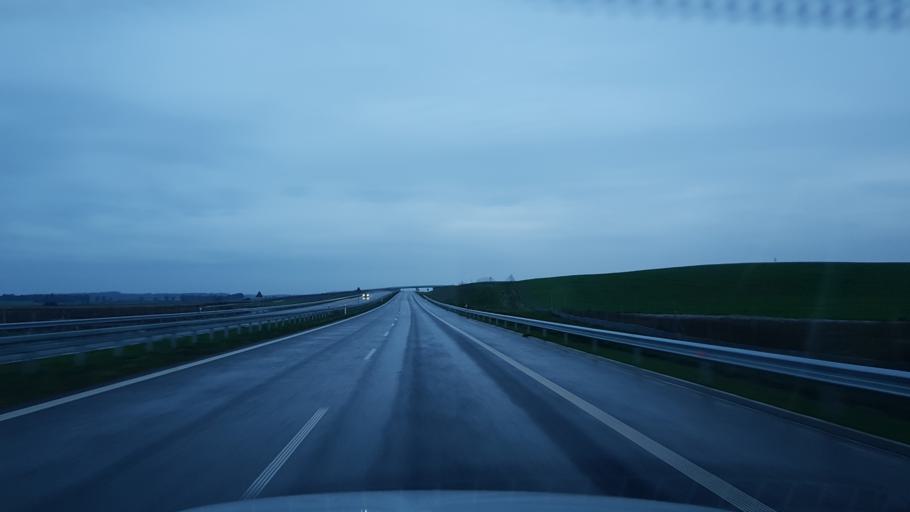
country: PL
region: West Pomeranian Voivodeship
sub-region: Powiat gryficki
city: Brojce
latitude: 53.9713
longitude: 15.4260
